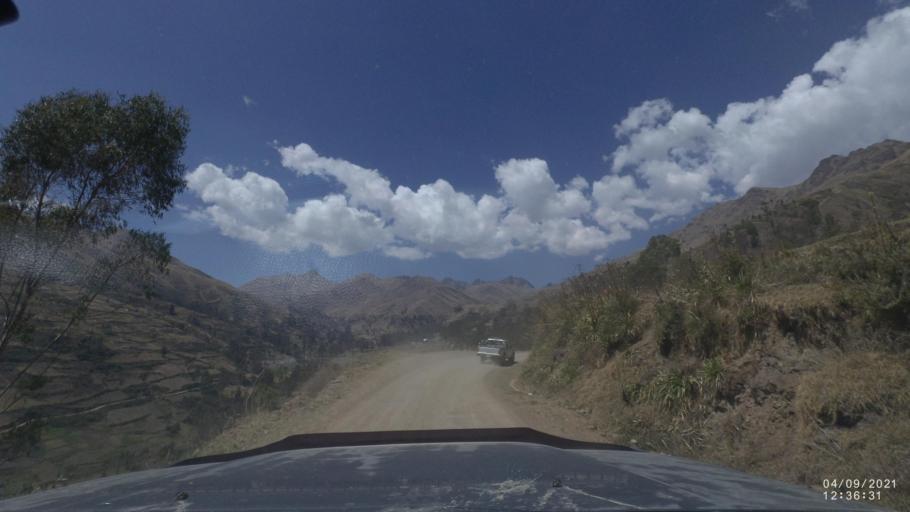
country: BO
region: Cochabamba
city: Colchani
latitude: -17.2241
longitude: -66.5065
